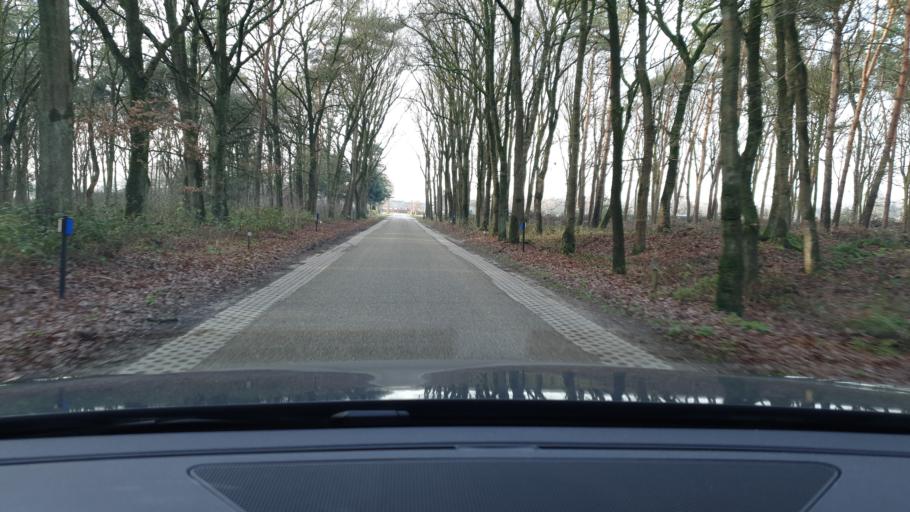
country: NL
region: Limburg
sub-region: Gemeente Peel en Maas
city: Maasbree
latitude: 51.4320
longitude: 6.0592
